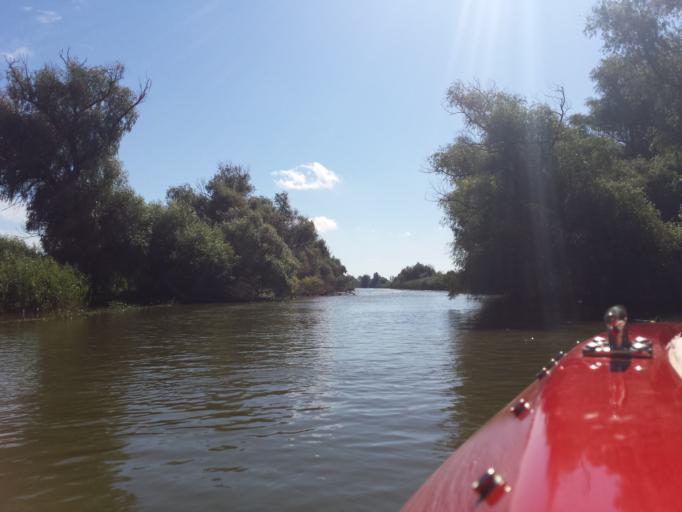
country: RO
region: Tulcea
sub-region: Comuna Mahmudia
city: Mahmudia
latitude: 45.2175
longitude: 29.1707
